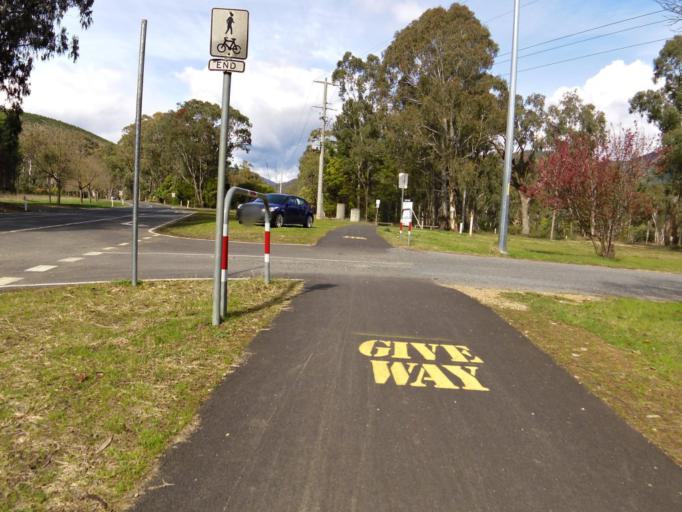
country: AU
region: Victoria
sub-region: Alpine
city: Mount Beauty
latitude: -36.7157
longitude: 146.9424
